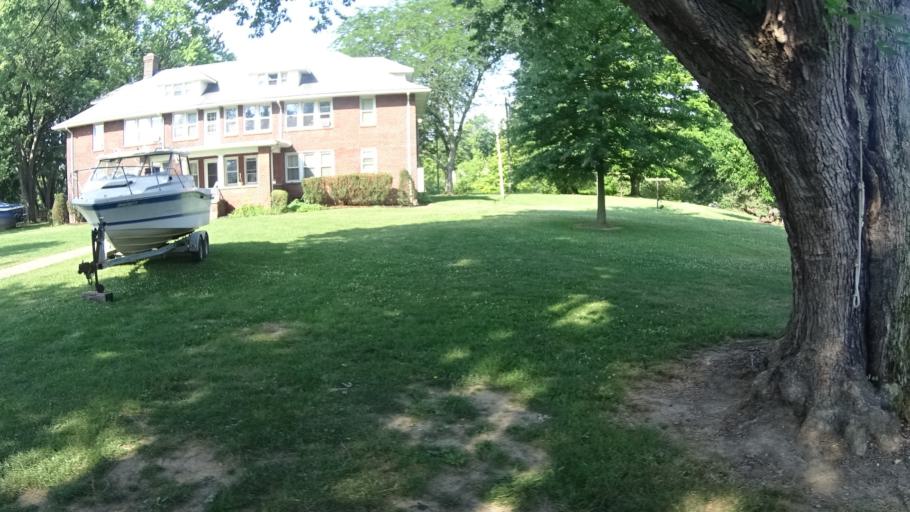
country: US
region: Ohio
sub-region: Lorain County
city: Vermilion
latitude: 41.3911
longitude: -82.4435
